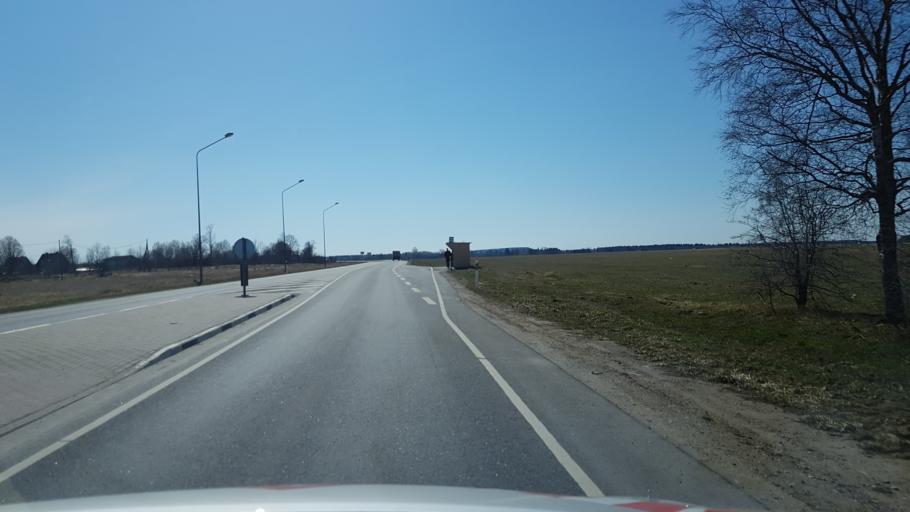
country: EE
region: Ida-Virumaa
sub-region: Johvi vald
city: Johvi
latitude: 59.3297
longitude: 27.4019
